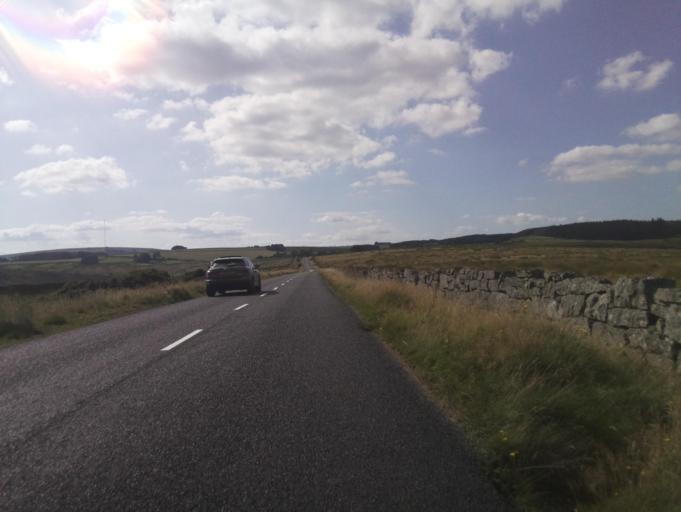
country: GB
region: England
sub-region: Devon
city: Yelverton
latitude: 50.5564
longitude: -3.9514
